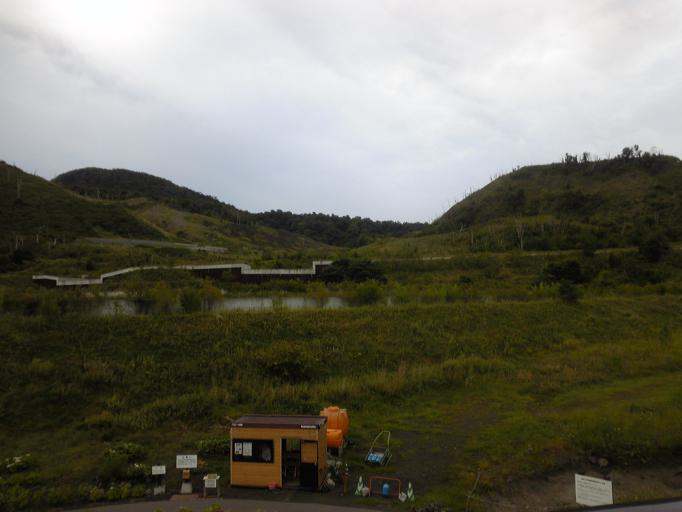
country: JP
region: Hokkaido
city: Date
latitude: 42.5636
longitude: 140.8147
